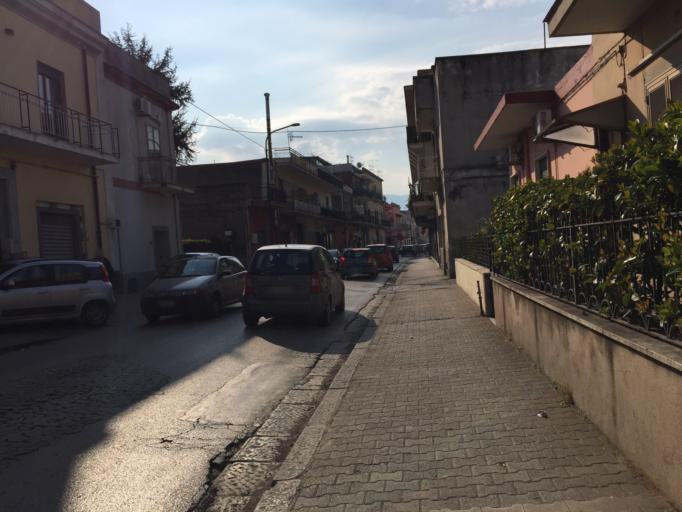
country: IT
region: Campania
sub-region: Provincia di Napoli
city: Pompei
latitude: 40.7527
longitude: 14.4995
